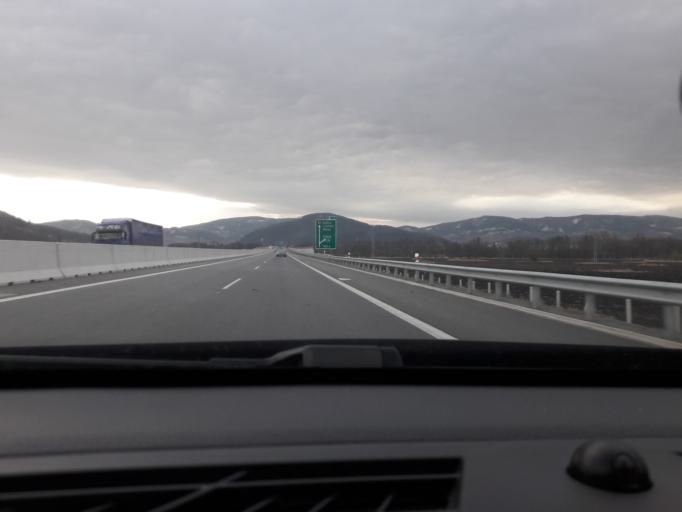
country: SK
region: Banskobystricky
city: Hrochot,Slovakia
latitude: 48.5583
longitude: 19.3171
